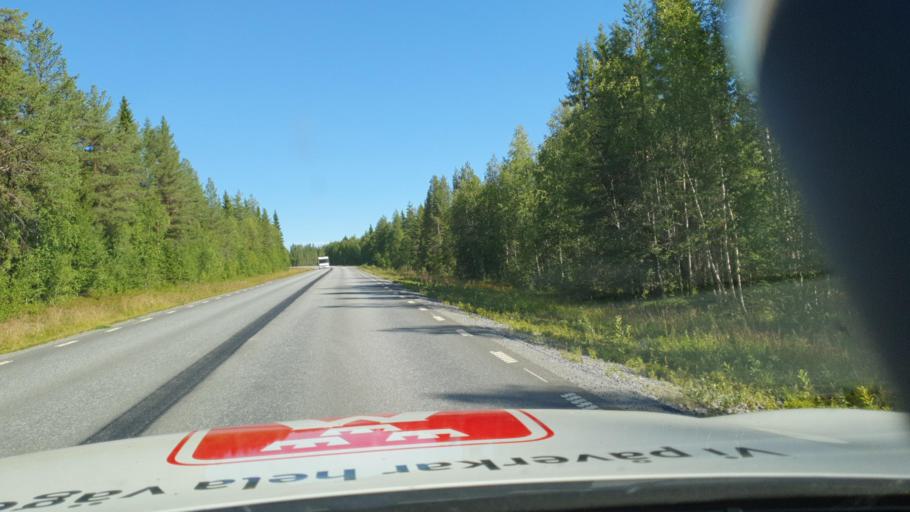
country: SE
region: Vaesterbotten
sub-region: Dorotea Kommun
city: Dorotea
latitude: 64.3080
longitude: 16.5991
